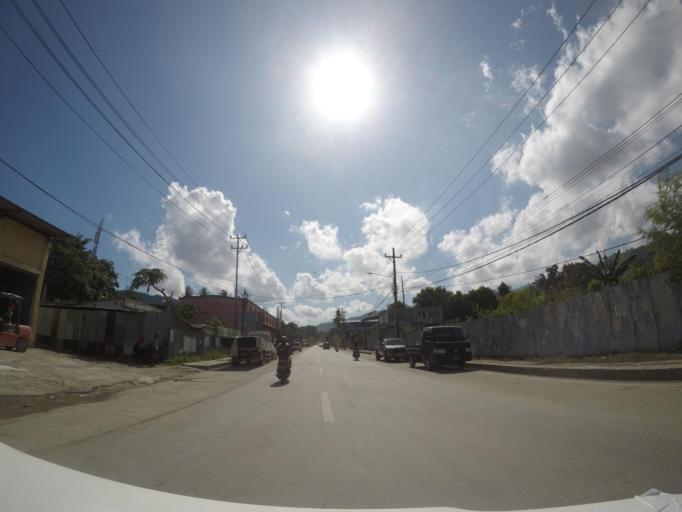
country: TL
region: Dili
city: Dili
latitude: -8.5609
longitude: 125.5987
